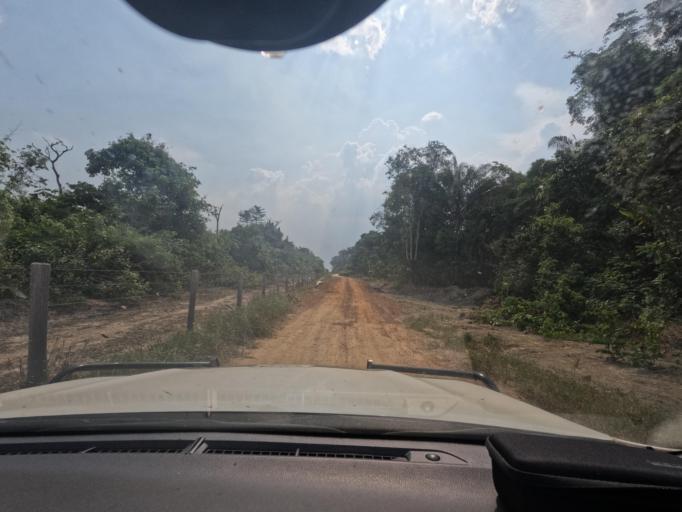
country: BR
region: Rondonia
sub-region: Porto Velho
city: Porto Velho
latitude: -8.7730
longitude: -63.2337
